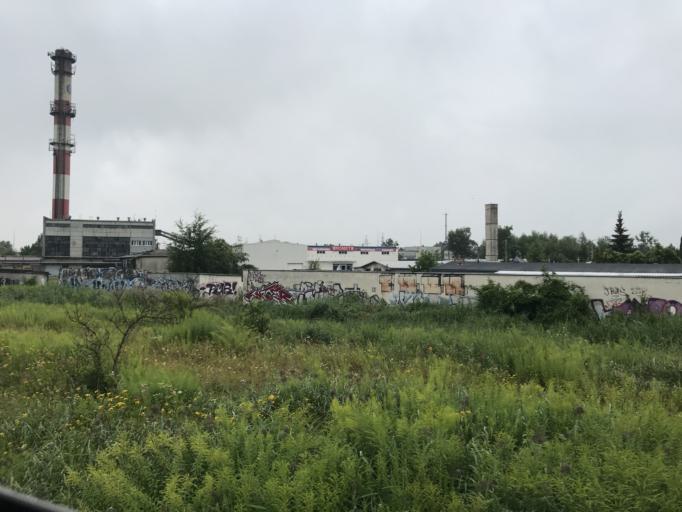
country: PL
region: Warmian-Masurian Voivodeship
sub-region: Powiat elblaski
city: Elblag
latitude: 54.1500
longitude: 19.4009
